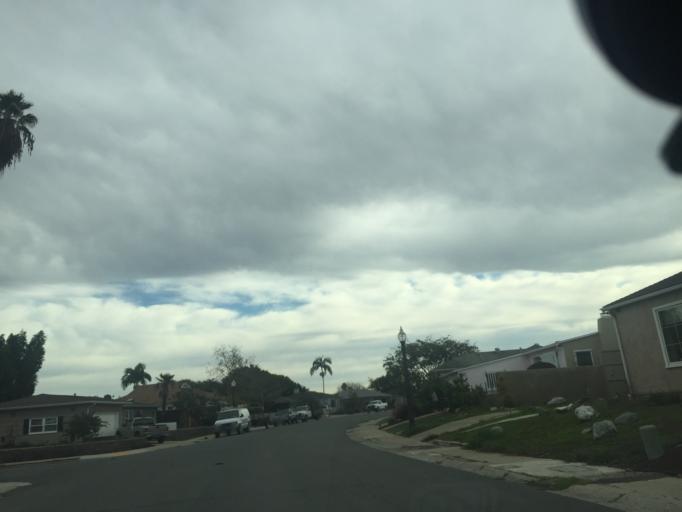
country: US
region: California
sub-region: San Diego County
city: Lemon Grove
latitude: 32.7674
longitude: -117.0907
